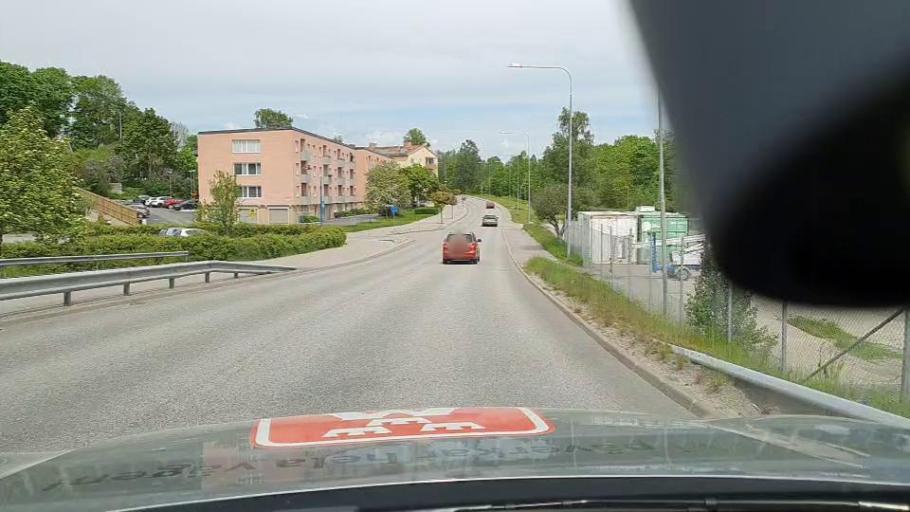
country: SE
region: Soedermanland
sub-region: Flens Kommun
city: Flen
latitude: 59.0534
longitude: 16.5951
